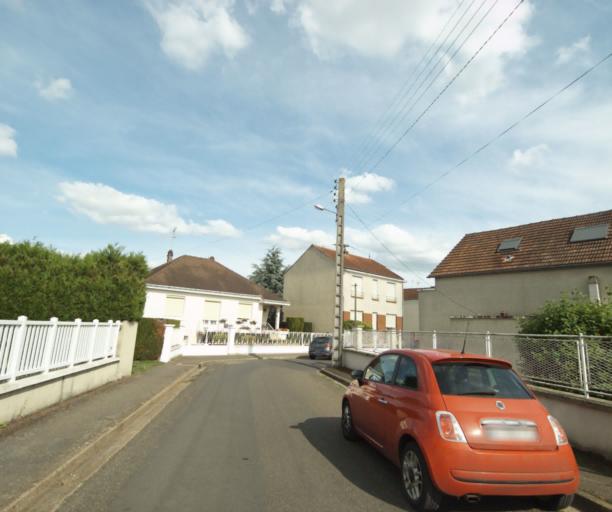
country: FR
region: Centre
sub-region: Departement d'Eure-et-Loir
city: Luisant
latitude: 48.4367
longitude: 1.4777
